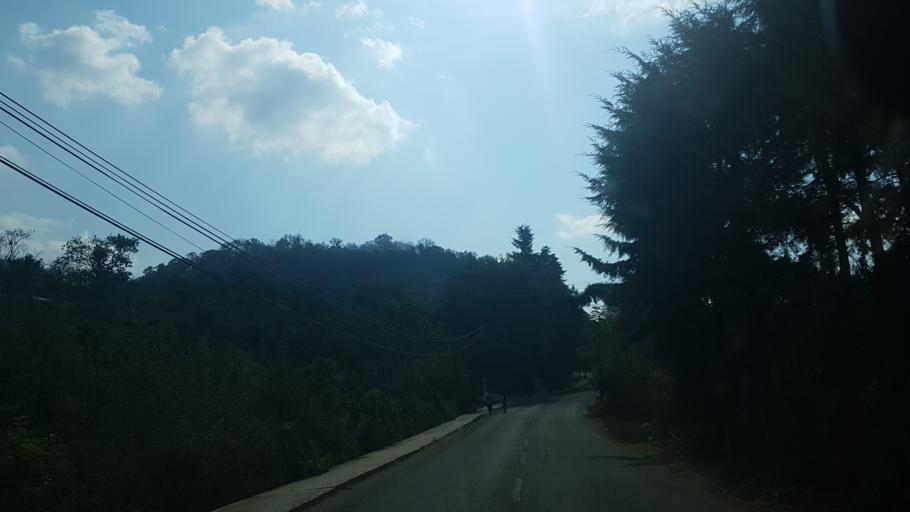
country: MX
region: Puebla
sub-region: Tochimilco
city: San Antonio Alpanocan
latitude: 18.8776
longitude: -98.7047
